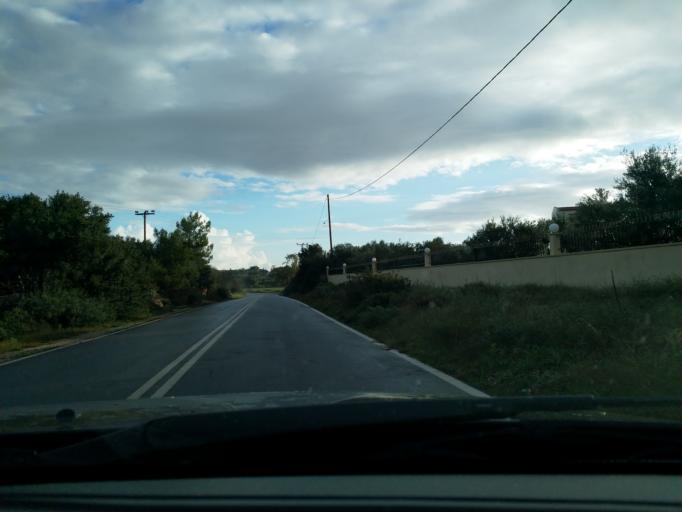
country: GR
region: Crete
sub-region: Nomos Chanias
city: Mouzouras
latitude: 35.5198
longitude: 24.1409
